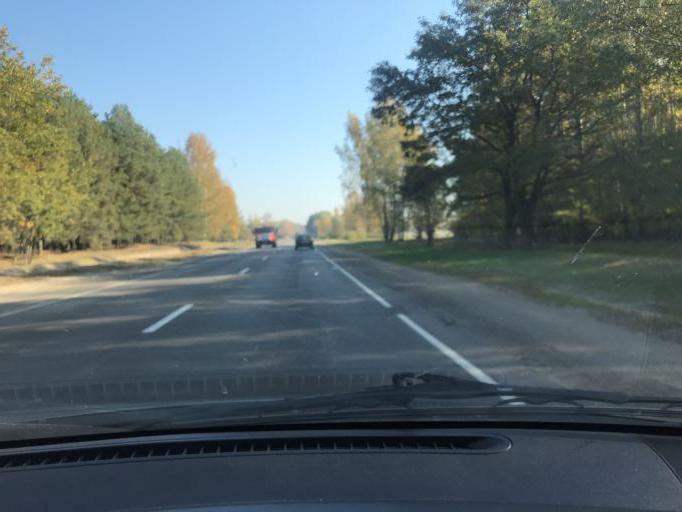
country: BY
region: Brest
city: Luninyets
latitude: 52.2759
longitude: 26.9403
